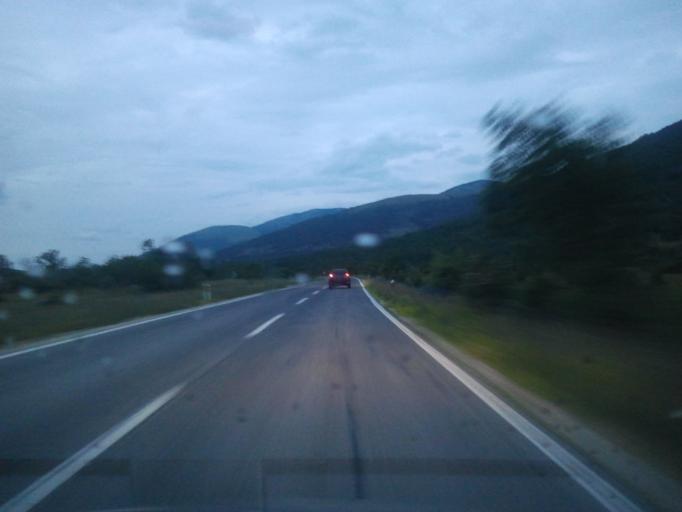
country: HR
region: Zadarska
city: Gracac
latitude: 44.4302
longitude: 15.8724
